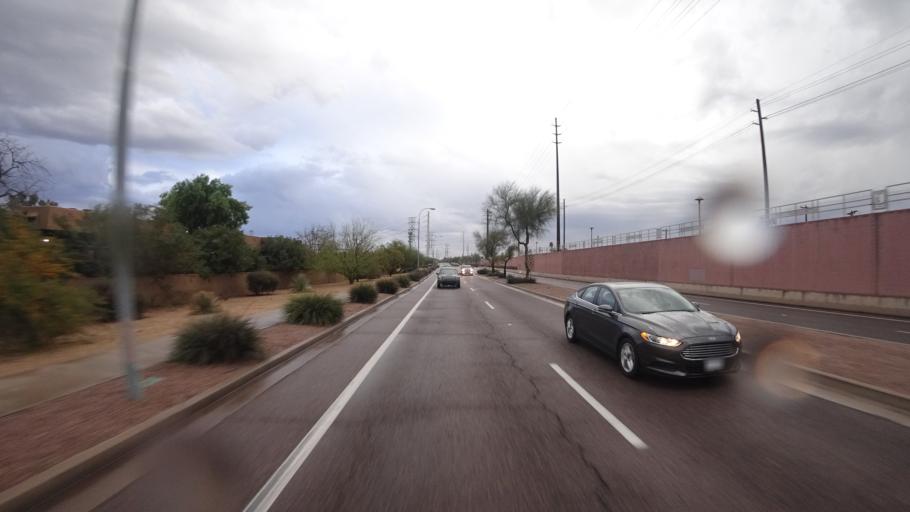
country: US
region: Arizona
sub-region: Maricopa County
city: Paradise Valley
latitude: 33.4856
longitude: -111.9427
